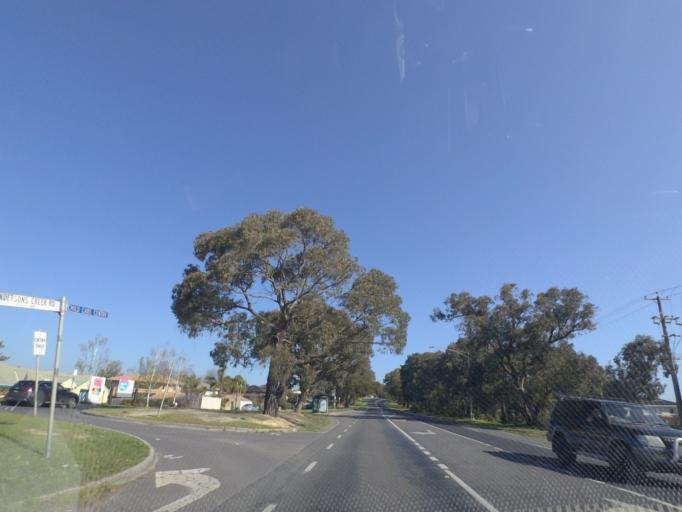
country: AU
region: Victoria
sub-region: Manningham
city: Donvale
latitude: -37.7703
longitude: 145.1707
